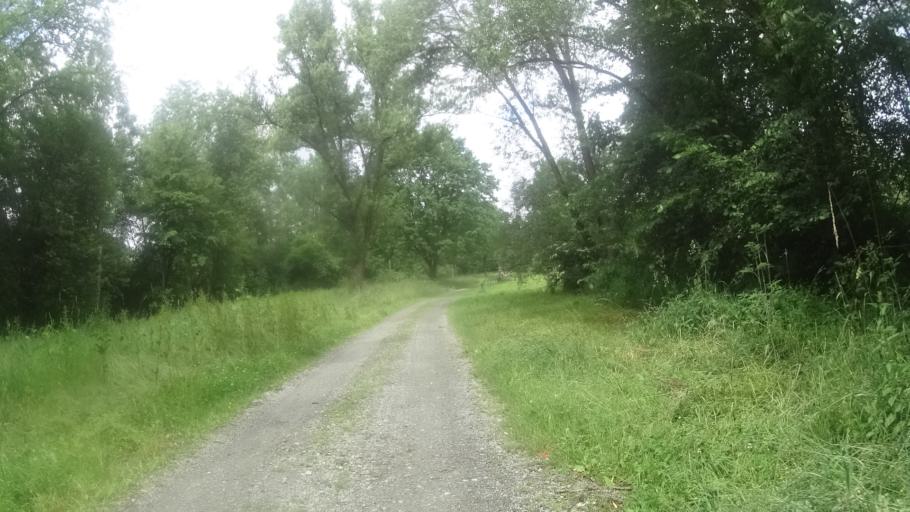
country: DE
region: Bavaria
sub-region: Lower Bavaria
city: Bad Birnbach
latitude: 48.4344
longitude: 13.0781
